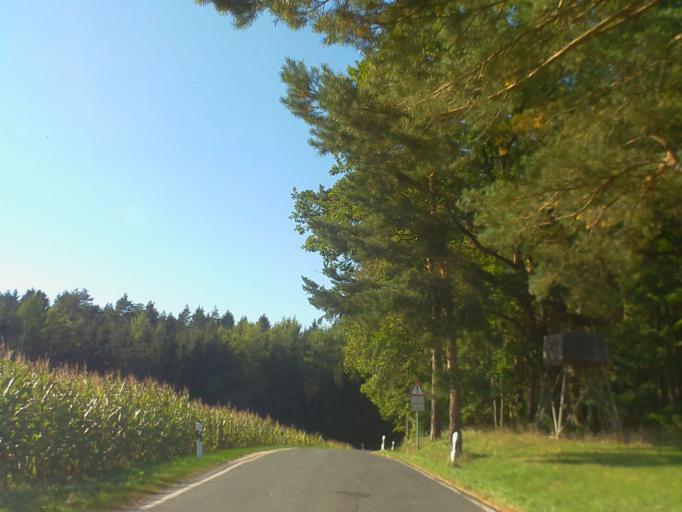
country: DE
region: Thuringia
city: Oberbodnitz
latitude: 50.7902
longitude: 11.6799
